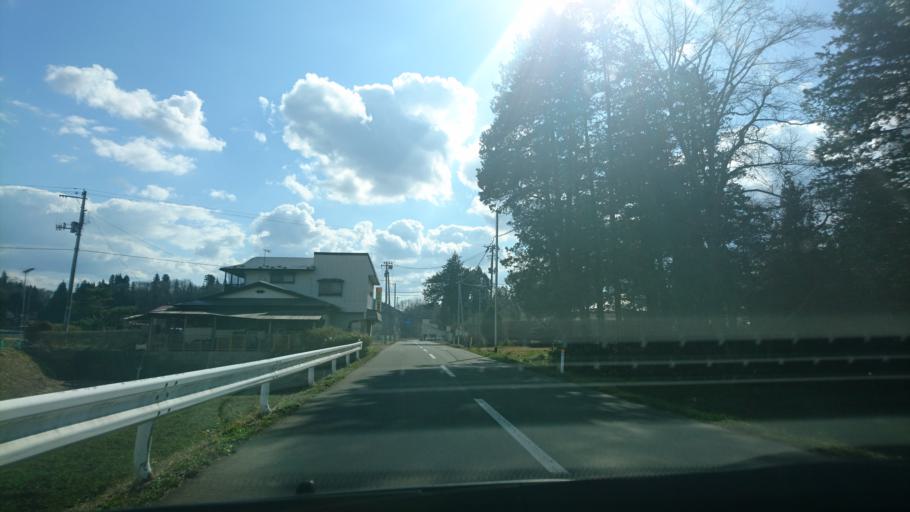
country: JP
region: Iwate
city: Kitakami
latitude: 39.2298
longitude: 141.1812
